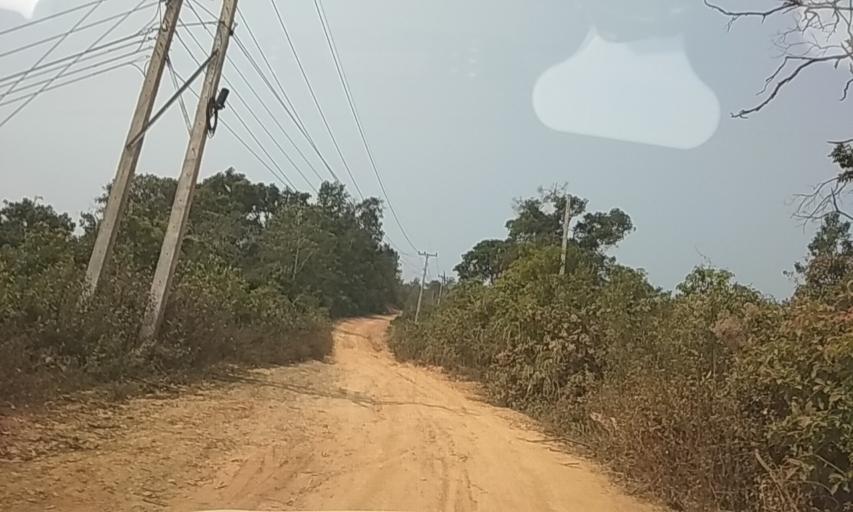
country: TH
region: Nan
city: Chaloem Phra Kiat
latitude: 20.0091
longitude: 101.1250
